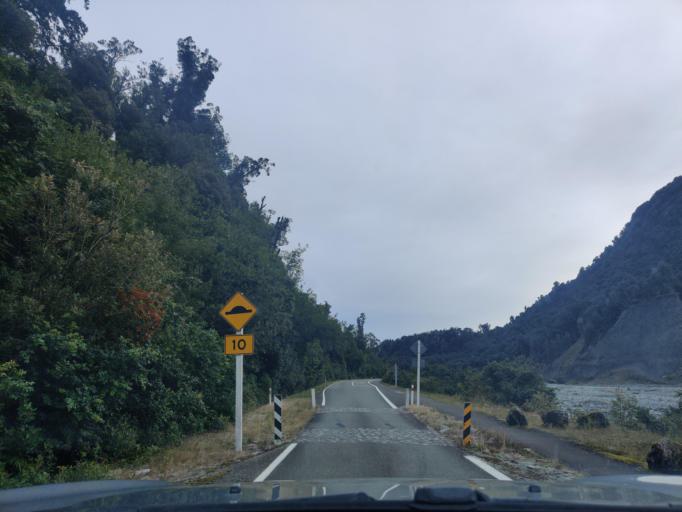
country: NZ
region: West Coast
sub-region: Westland District
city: Hokitika
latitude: -43.4000
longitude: 170.1803
